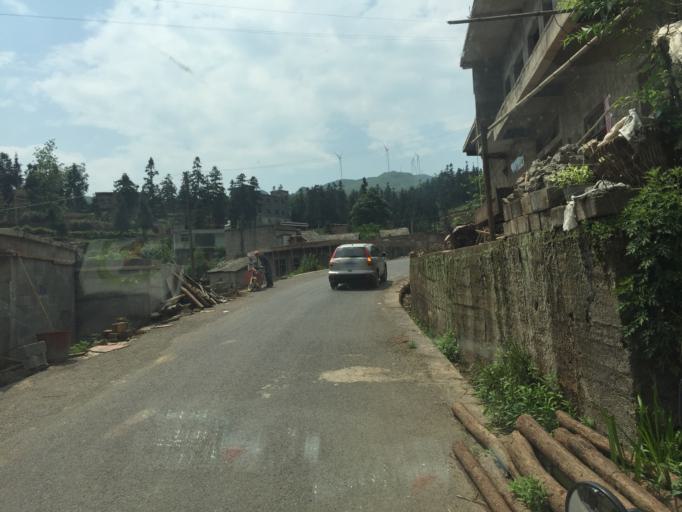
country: CN
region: Guangxi Zhuangzu Zizhiqu
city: Xinzhou
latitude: 25.6947
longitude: 105.2309
